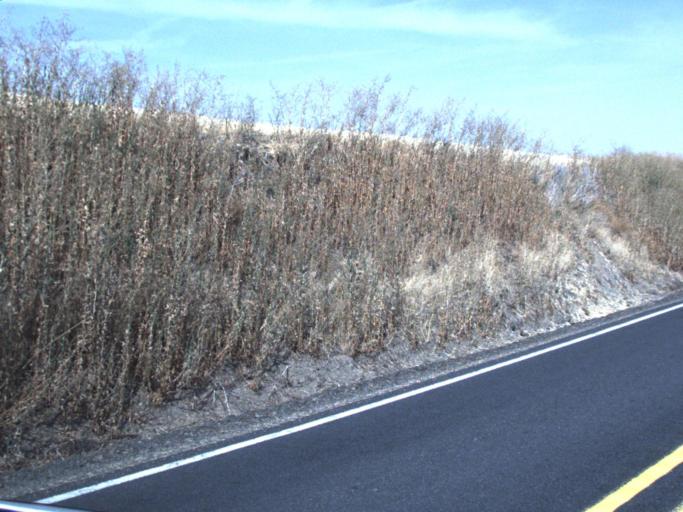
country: US
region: Washington
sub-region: Whitman County
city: Colfax
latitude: 47.1706
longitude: -117.2028
